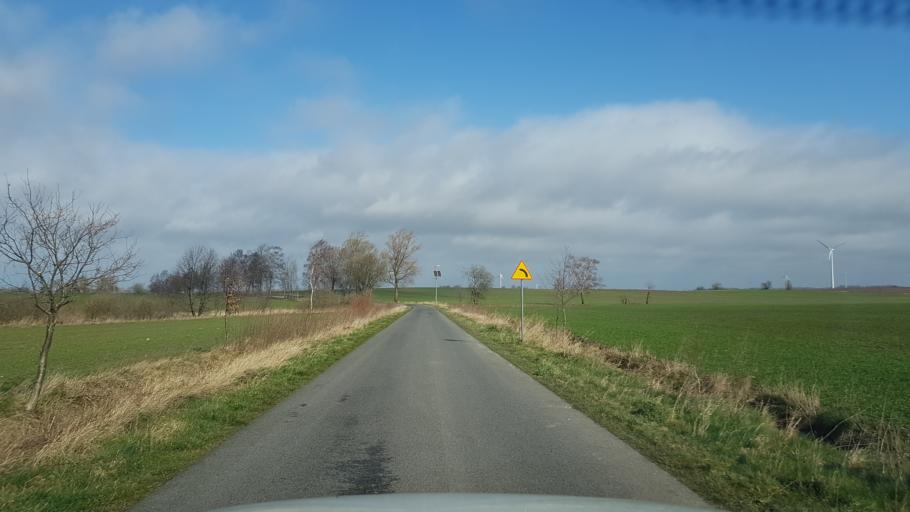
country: PL
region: West Pomeranian Voivodeship
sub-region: Powiat slawienski
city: Slawno
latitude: 54.4972
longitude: 16.6520
